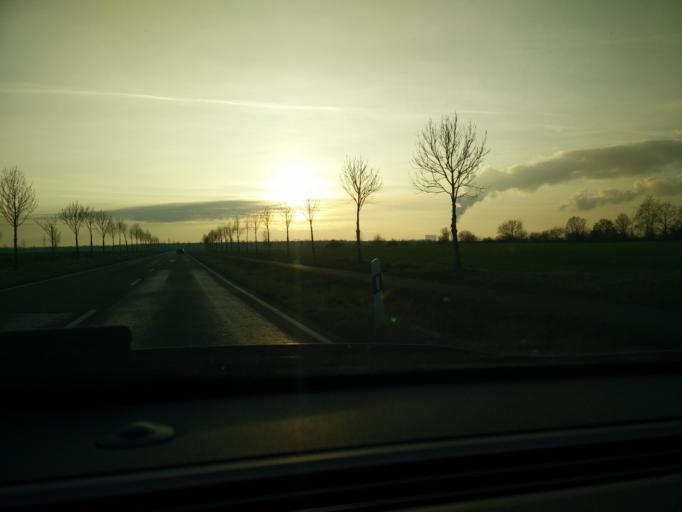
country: DE
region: Saxony
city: Espenhain
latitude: 51.2198
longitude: 12.4590
